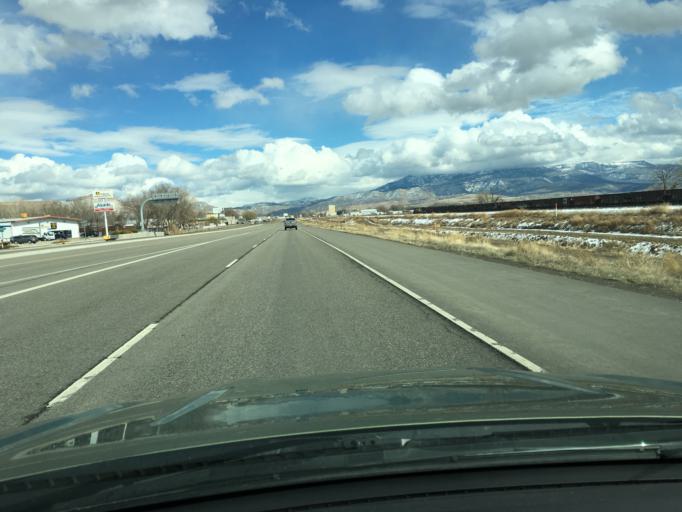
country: US
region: Colorado
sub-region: Mesa County
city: Fruitvale
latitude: 39.0734
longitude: -108.5124
